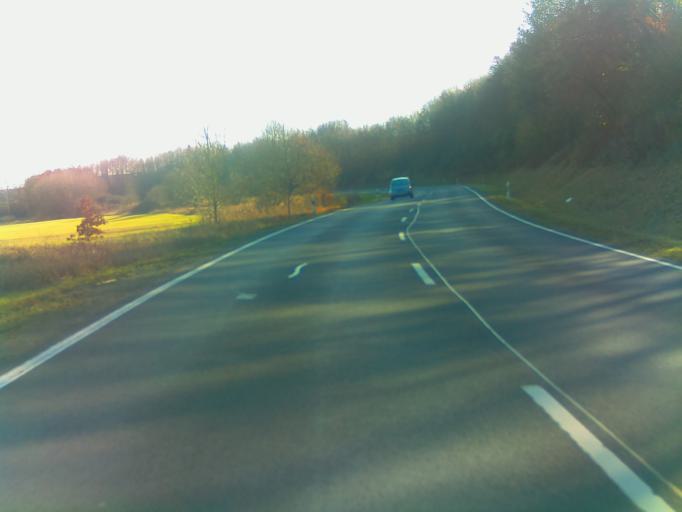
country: DE
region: Bavaria
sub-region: Regierungsbezirk Unterfranken
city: Wuelfershausen
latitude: 50.3300
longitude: 10.3204
